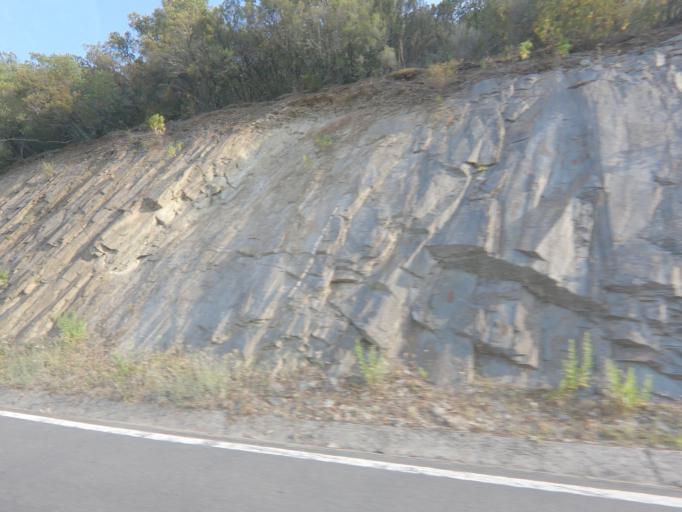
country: PT
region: Viseu
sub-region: Tabuaco
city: Tabuaco
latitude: 41.1487
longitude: -7.6199
